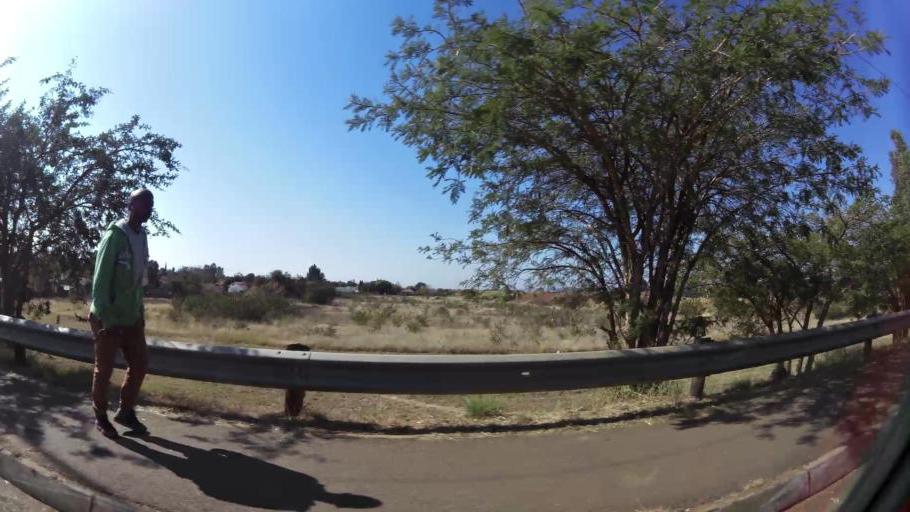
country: ZA
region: North-West
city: Ga-Rankuwa
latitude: -25.6545
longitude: 28.1021
